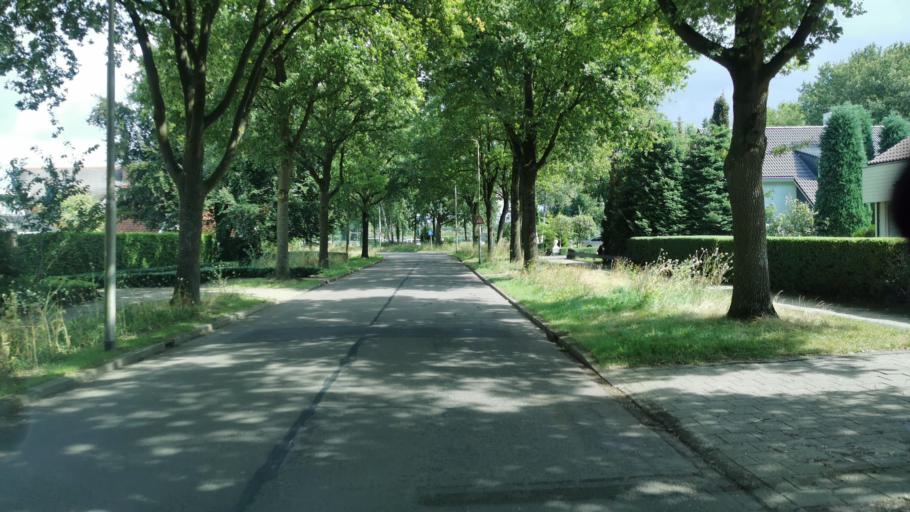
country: NL
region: Overijssel
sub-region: Gemeente Losser
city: Losser
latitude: 52.2709
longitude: 7.0141
